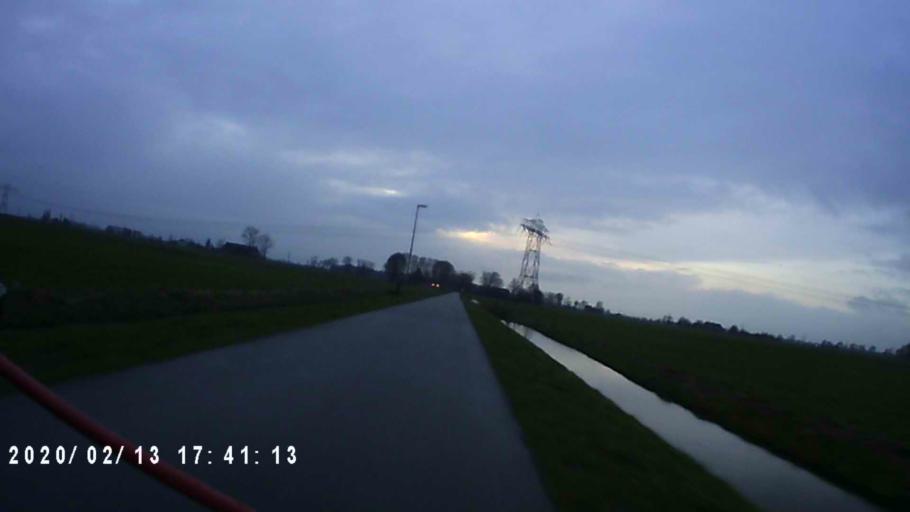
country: NL
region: Groningen
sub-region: Gemeente Zuidhorn
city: Aduard
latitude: 53.2292
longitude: 6.4978
